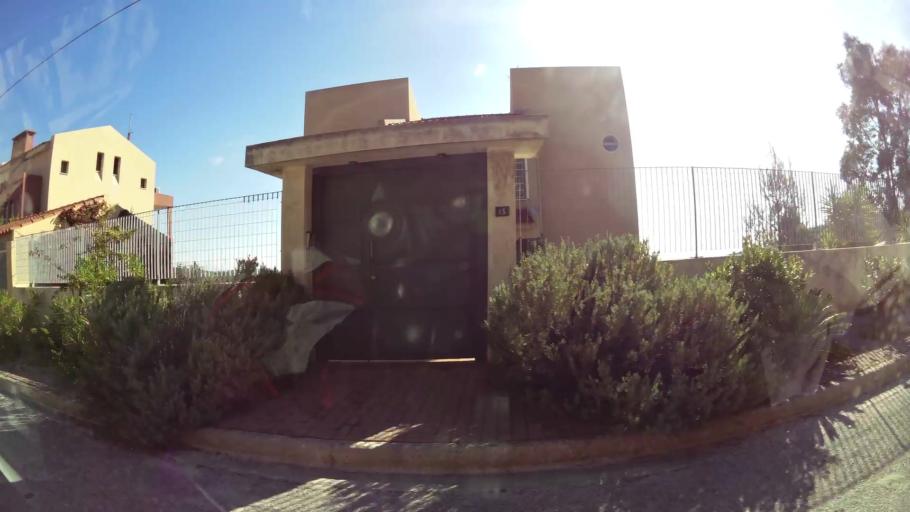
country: GR
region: Attica
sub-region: Nomarchia Anatolikis Attikis
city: Dhrafi
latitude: 38.0319
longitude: 23.8972
